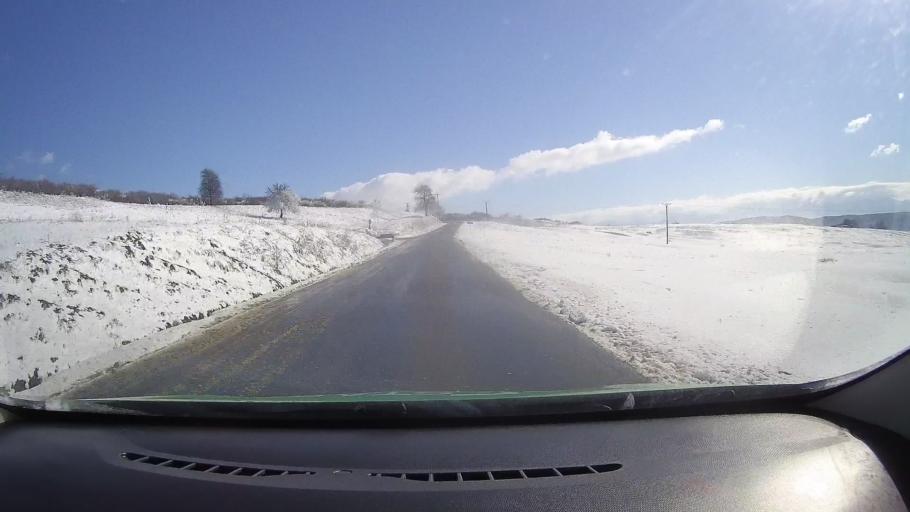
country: RO
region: Sibiu
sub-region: Comuna Rosia
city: Rosia
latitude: 45.8079
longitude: 24.2924
